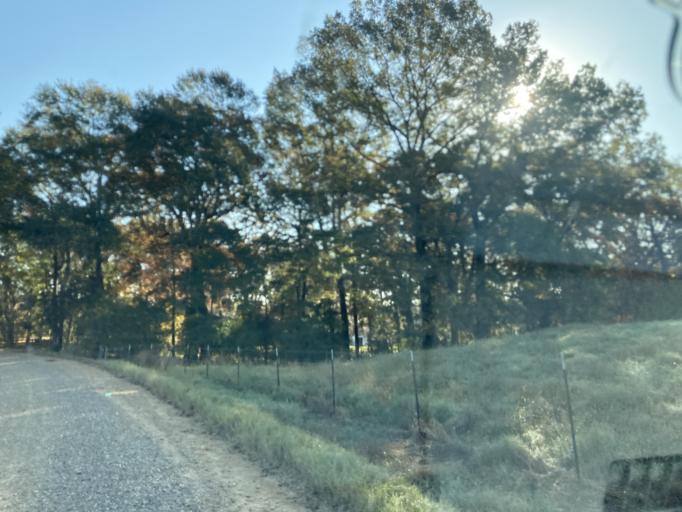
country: US
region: Mississippi
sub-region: Madison County
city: Kearney Park
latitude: 32.7050
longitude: -90.2660
